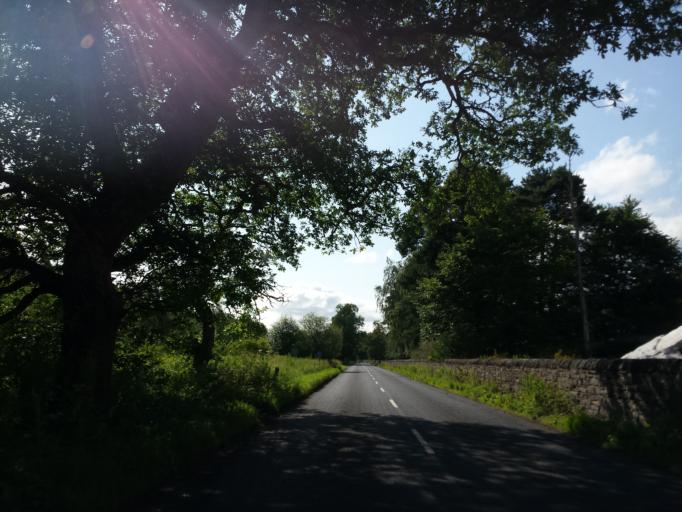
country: GB
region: Scotland
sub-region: Perth and Kinross
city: Pitlochry
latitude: 56.7664
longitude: -3.8572
